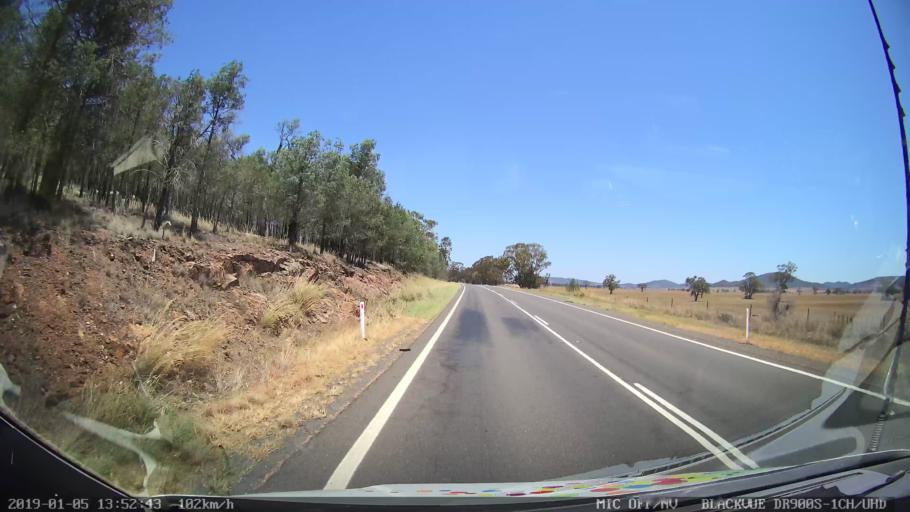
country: AU
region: New South Wales
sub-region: Gunnedah
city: Gunnedah
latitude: -31.0642
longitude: 150.2769
